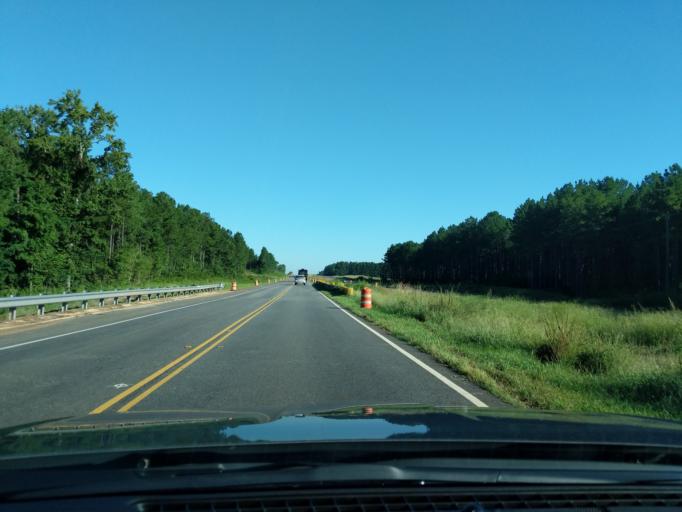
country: US
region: Georgia
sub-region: McDuffie County
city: Thomson
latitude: 33.5526
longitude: -82.5116
